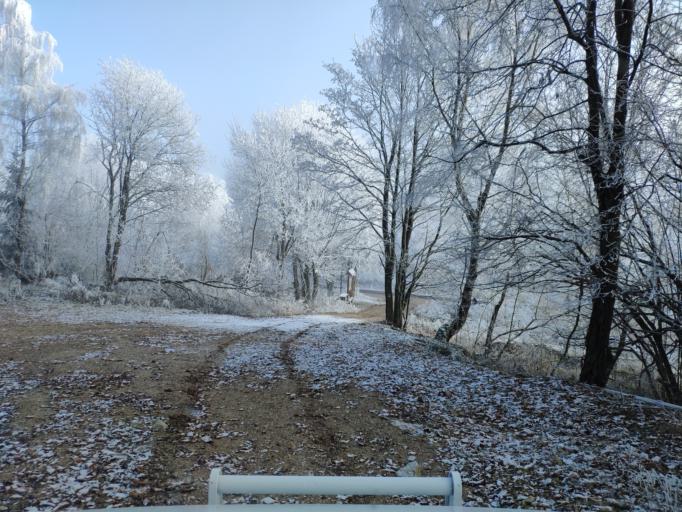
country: SK
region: Kosicky
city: Dobsina
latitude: 48.8130
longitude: 20.4796
